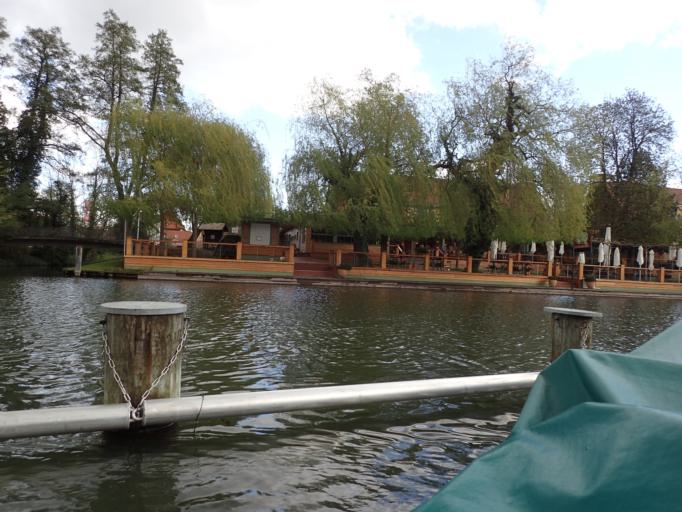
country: DE
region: Brandenburg
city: Luebben
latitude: 51.9392
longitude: 13.8956
